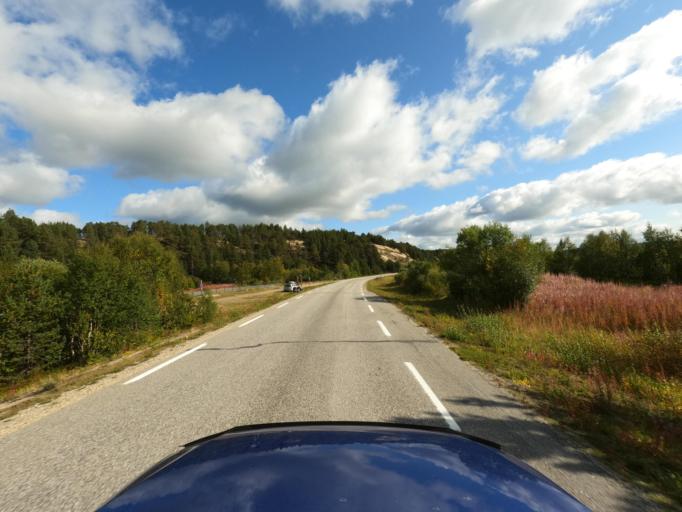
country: NO
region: Finnmark Fylke
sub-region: Karasjok
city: Karasjohka
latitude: 69.4447
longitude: 25.2016
